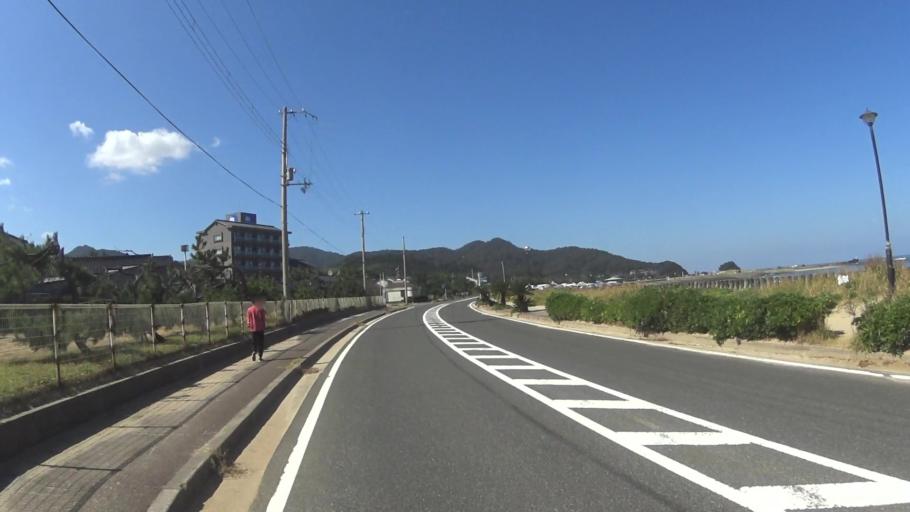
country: JP
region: Kyoto
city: Miyazu
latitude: 35.6890
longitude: 135.0256
